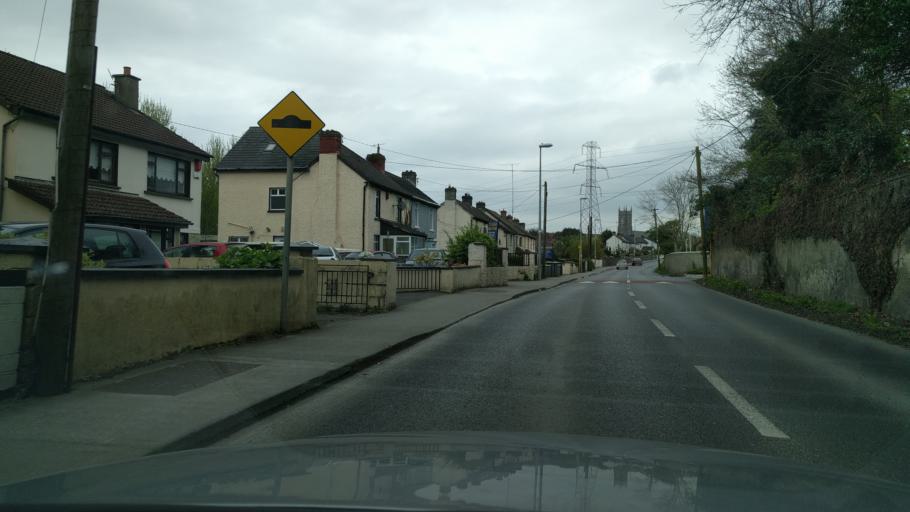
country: IE
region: Leinster
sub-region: South Dublin
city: Saggart
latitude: 53.2818
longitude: -6.4486
